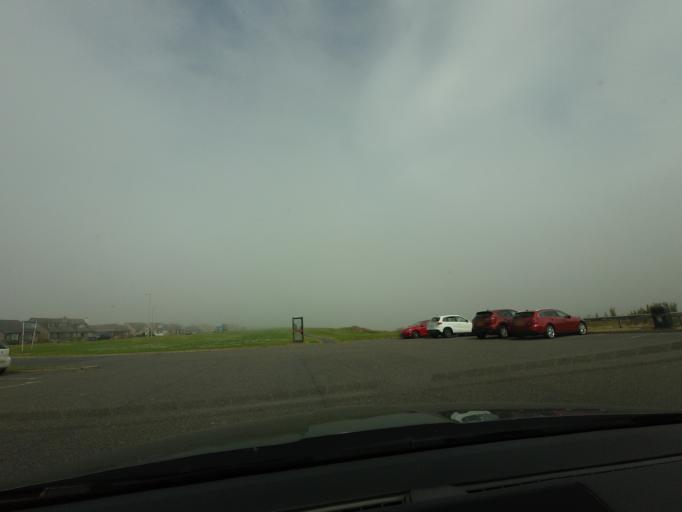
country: GB
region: Scotland
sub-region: Aberdeenshire
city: Peterhead
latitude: 57.4972
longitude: -1.7960
